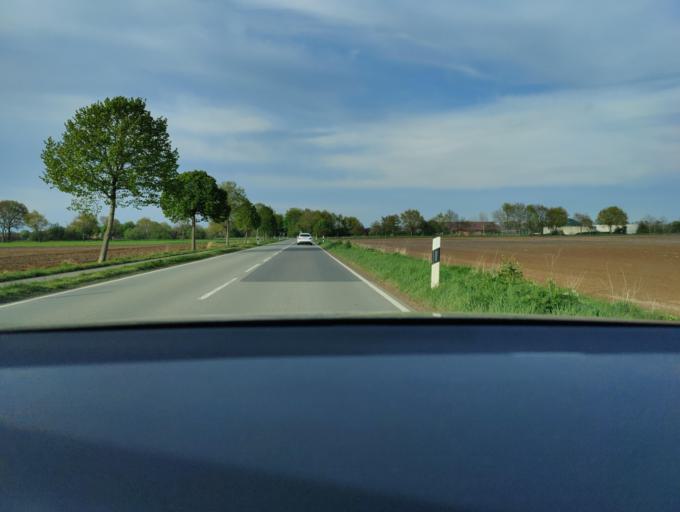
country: DE
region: Lower Saxony
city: Wietmarschen
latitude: 52.4799
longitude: 7.1153
